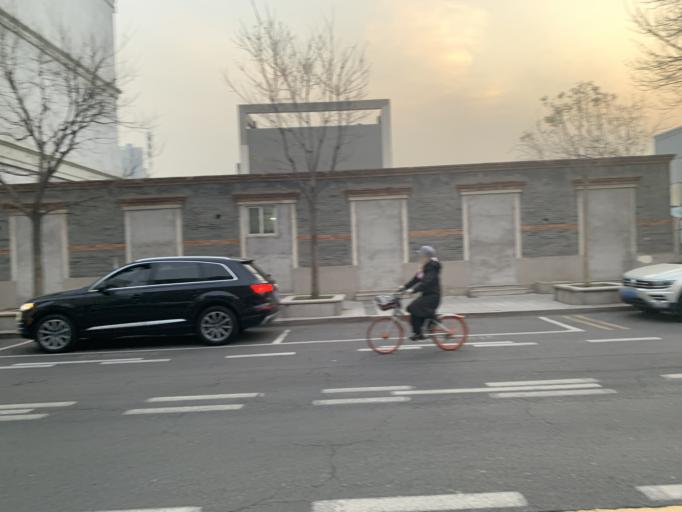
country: CN
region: Tianjin Shi
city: Hongshunli
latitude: 39.1523
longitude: 117.1864
